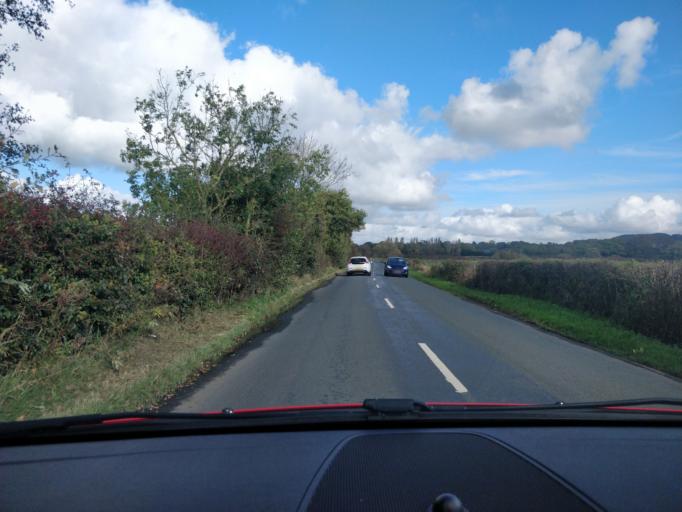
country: GB
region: England
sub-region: Lancashire
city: Parbold
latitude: 53.6092
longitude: -2.7885
